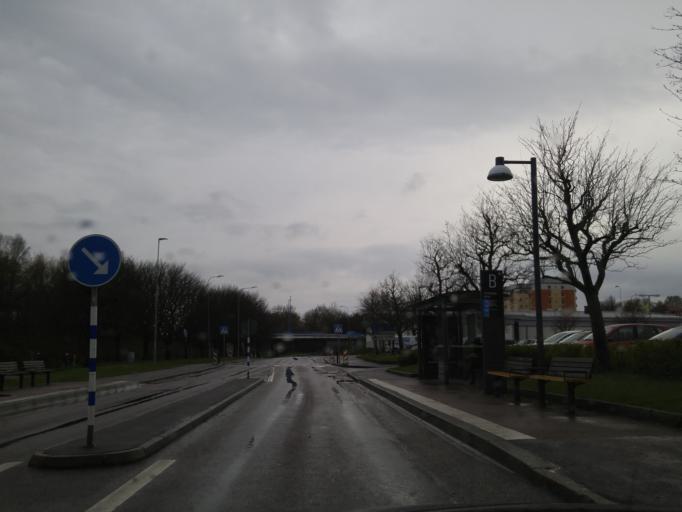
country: SE
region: Vaestra Goetaland
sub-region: Goteborg
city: Majorna
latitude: 57.6611
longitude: 11.9344
